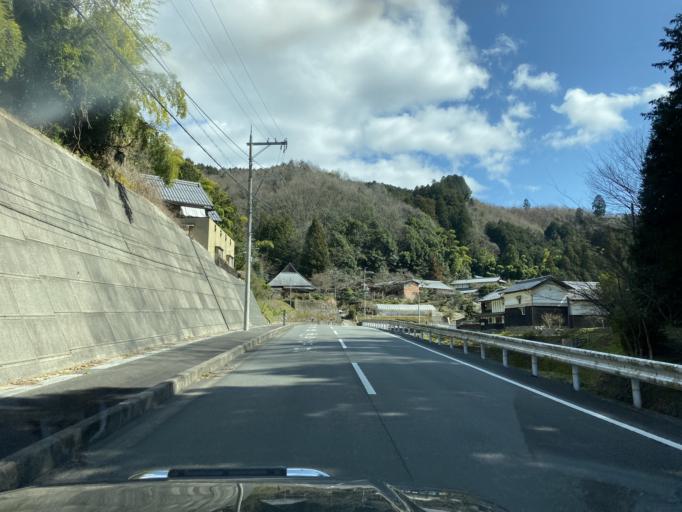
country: JP
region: Nara
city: Nara-shi
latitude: 34.6953
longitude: 135.9516
